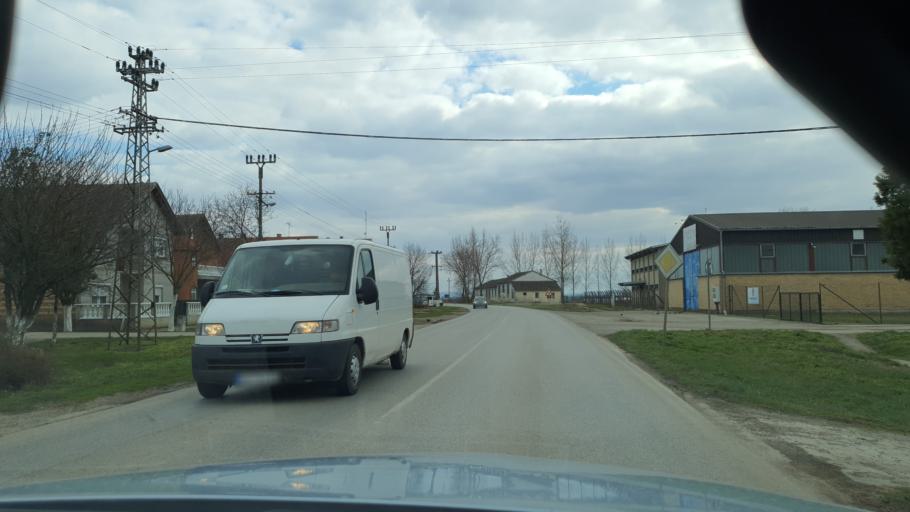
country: RS
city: Obrovac
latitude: 45.4118
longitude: 19.4051
